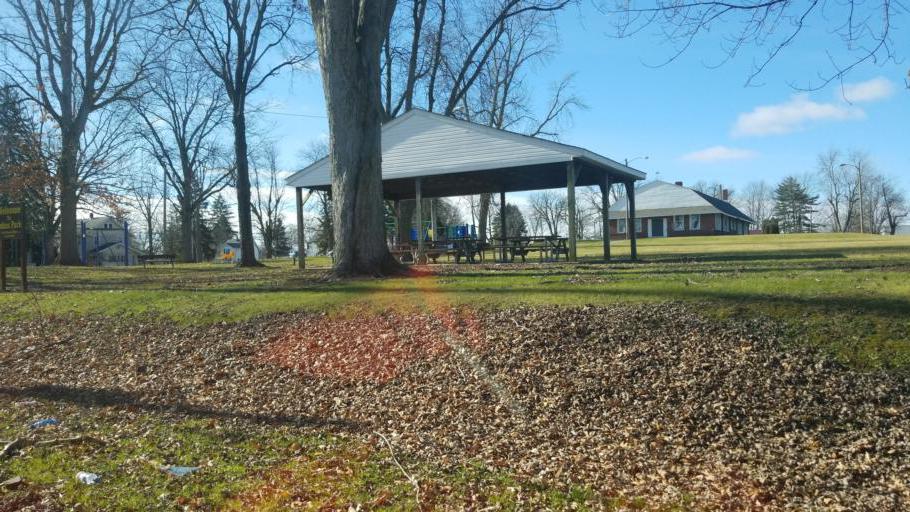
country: US
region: Ohio
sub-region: Richland County
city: Mansfield
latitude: 40.7753
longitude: -82.5242
